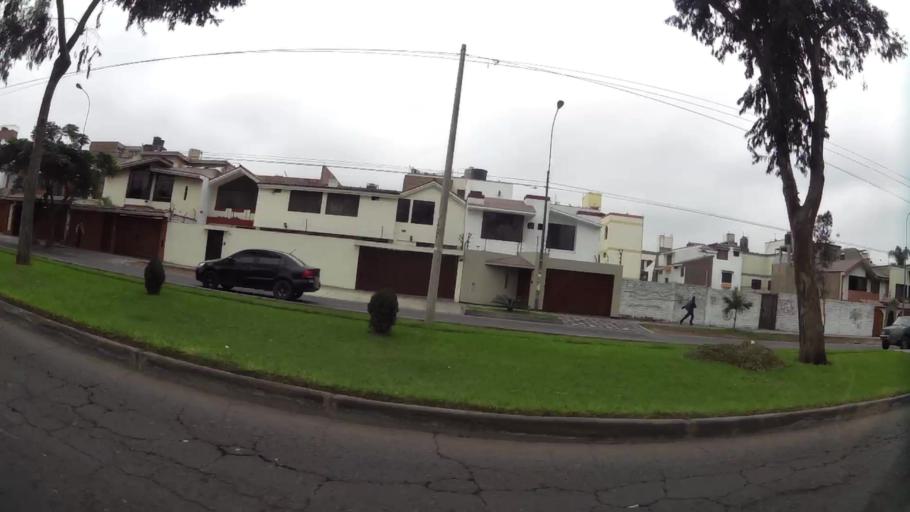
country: PE
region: Lima
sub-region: Lima
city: La Molina
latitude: -12.0701
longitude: -76.9484
